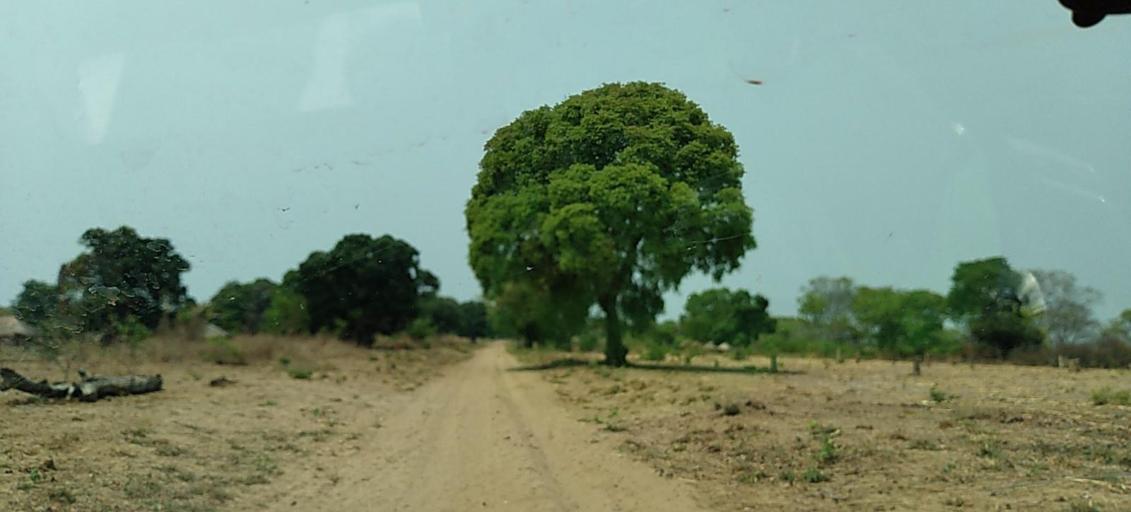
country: ZM
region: Western
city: Lukulu
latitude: -13.9964
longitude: 23.2337
